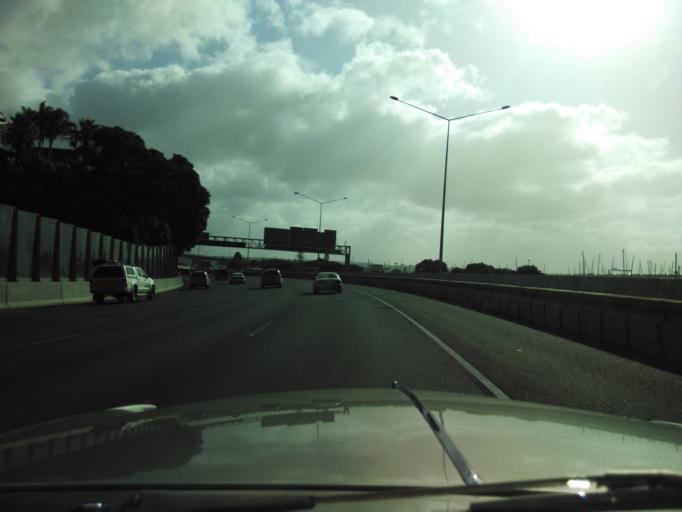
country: NZ
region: Auckland
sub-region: Auckland
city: Auckland
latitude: -36.8412
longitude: 174.7453
